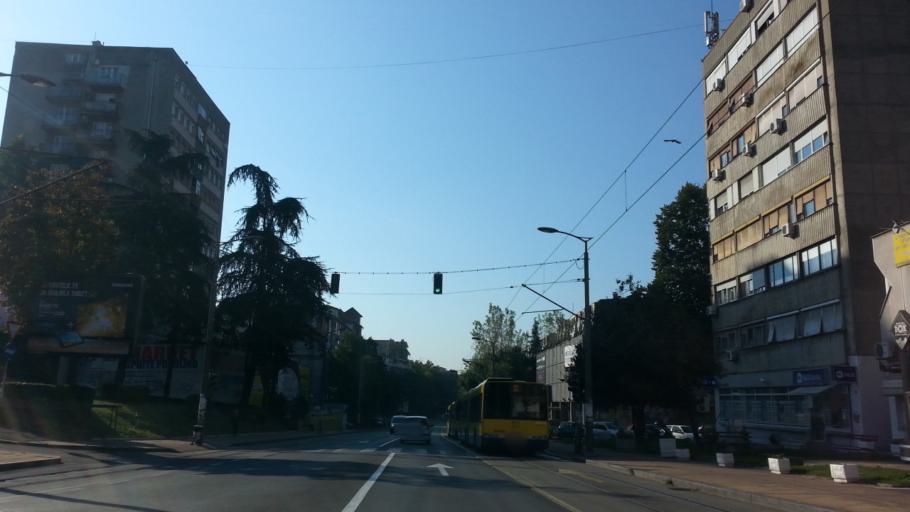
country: RS
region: Central Serbia
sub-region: Belgrade
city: Cukarica
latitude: 44.7740
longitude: 20.4137
